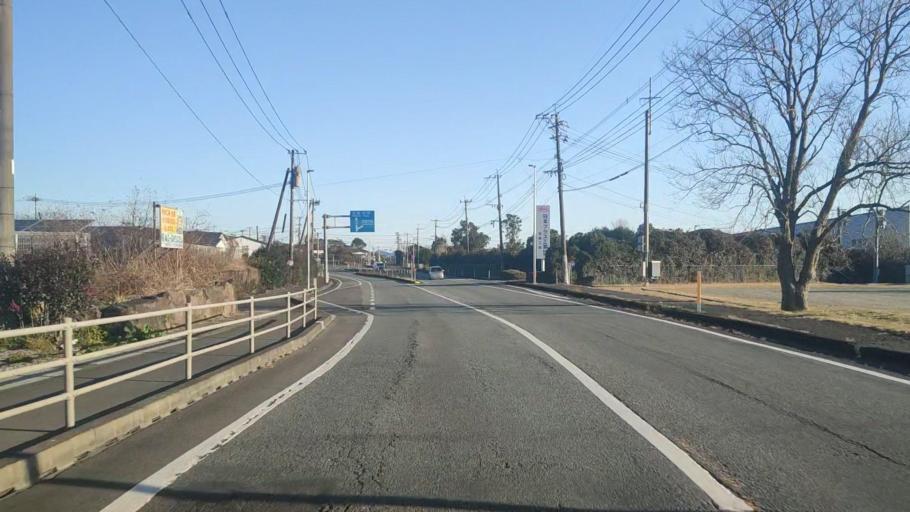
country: JP
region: Miyazaki
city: Takanabe
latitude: 32.2439
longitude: 131.5508
